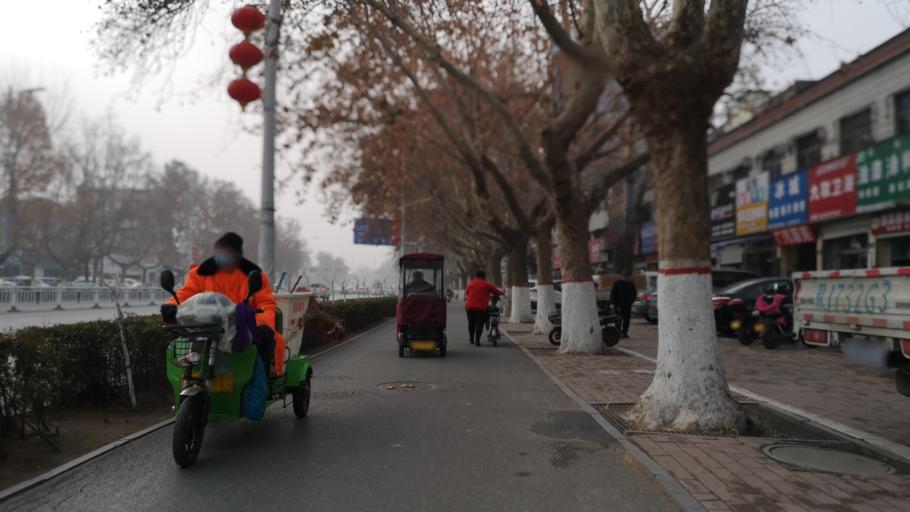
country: CN
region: Henan Sheng
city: Zhongyuanlu
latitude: 35.7739
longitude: 115.0398
